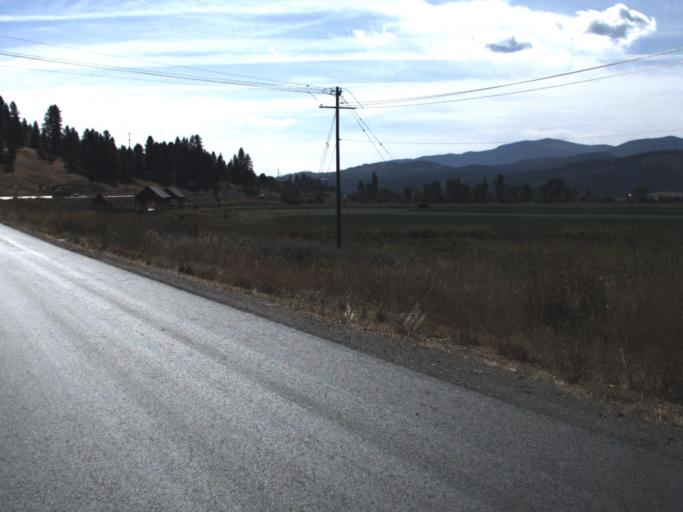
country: US
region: Washington
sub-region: Stevens County
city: Colville
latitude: 48.5185
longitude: -117.9014
